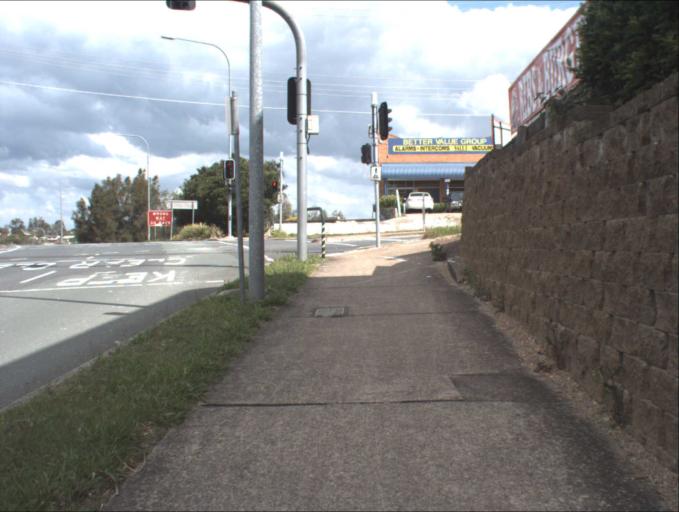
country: AU
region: Queensland
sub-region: Brisbane
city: Sunnybank Hills
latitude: -27.6612
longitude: 153.0362
